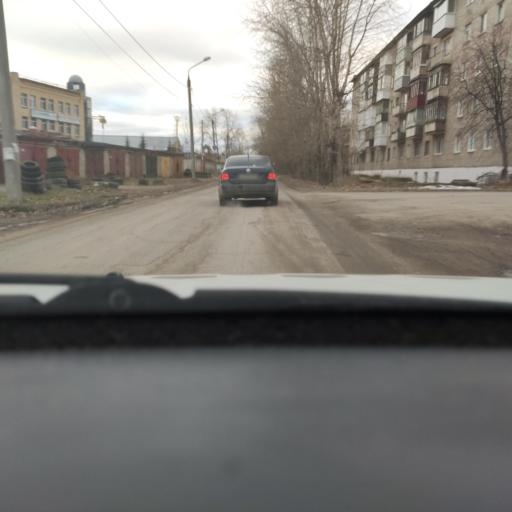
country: RU
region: Perm
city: Perm
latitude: 57.9743
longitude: 56.2786
